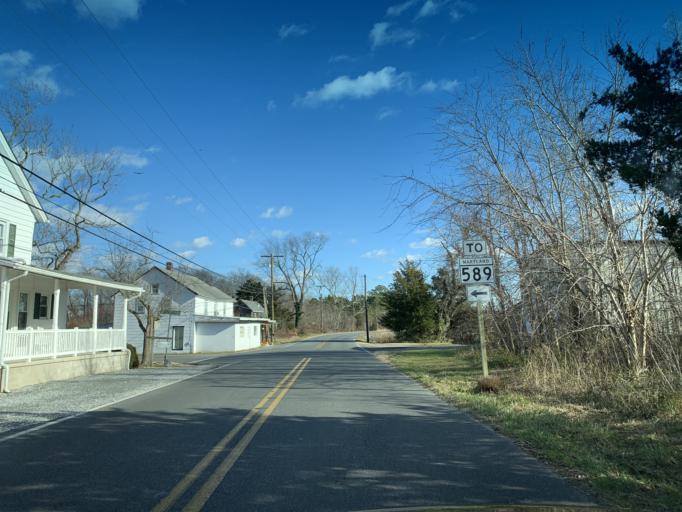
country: US
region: Maryland
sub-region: Worcester County
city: Ocean Pines
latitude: 38.3487
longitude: -75.1714
